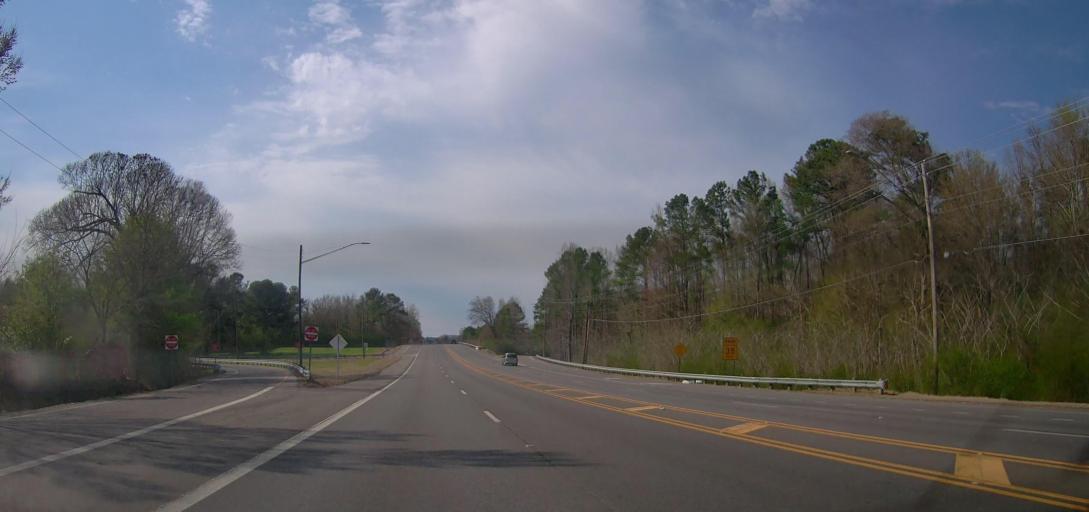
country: US
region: Alabama
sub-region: Jefferson County
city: Forestdale
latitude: 33.5457
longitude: -86.8766
